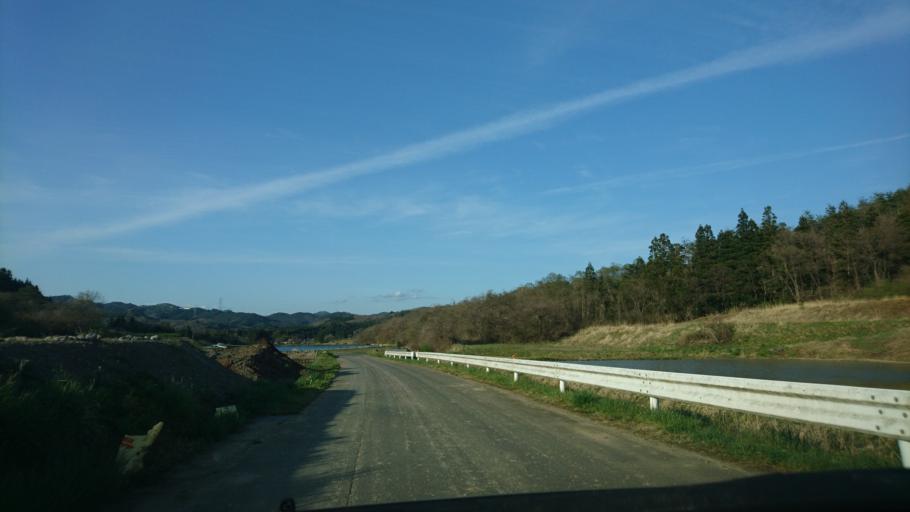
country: JP
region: Iwate
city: Ichinoseki
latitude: 38.8937
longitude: 141.2209
